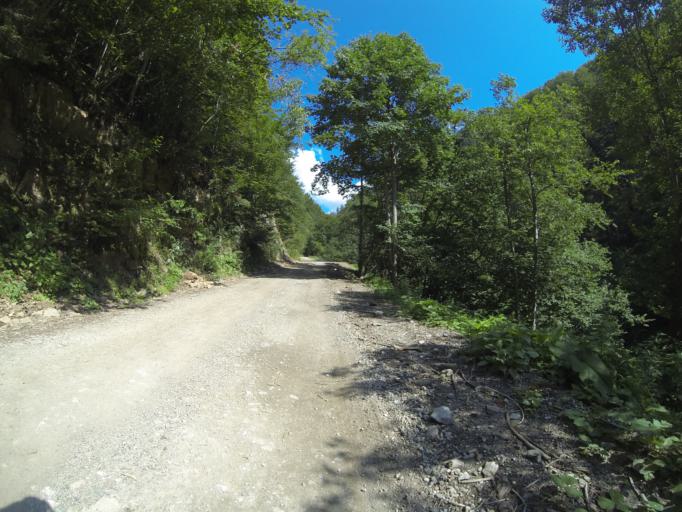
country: RO
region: Valcea
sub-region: Comuna Costesti
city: Bistrita
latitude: 45.2461
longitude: 23.9948
